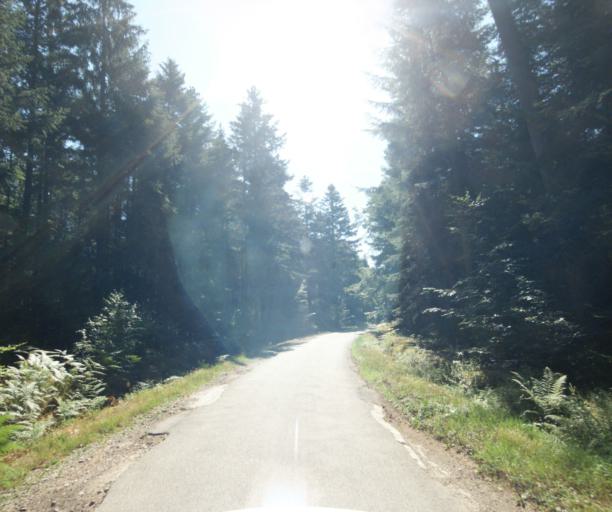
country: FR
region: Lorraine
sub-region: Departement des Vosges
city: Epinal
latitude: 48.1575
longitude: 6.4746
